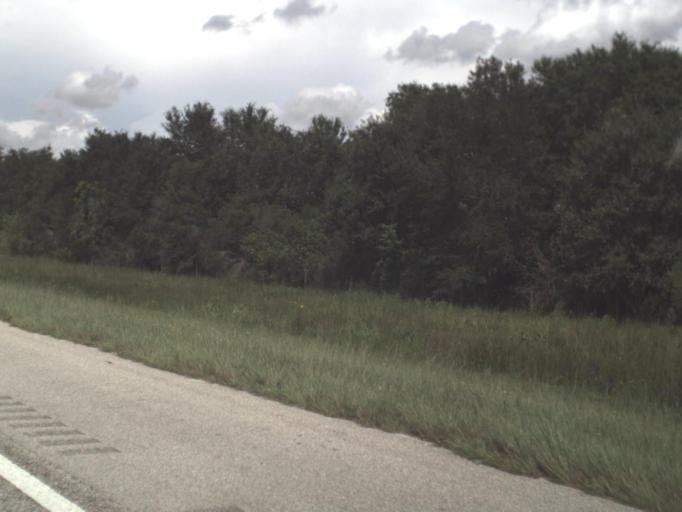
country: US
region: Florida
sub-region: Lee County
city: Suncoast Estates
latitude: 26.7906
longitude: -81.9040
